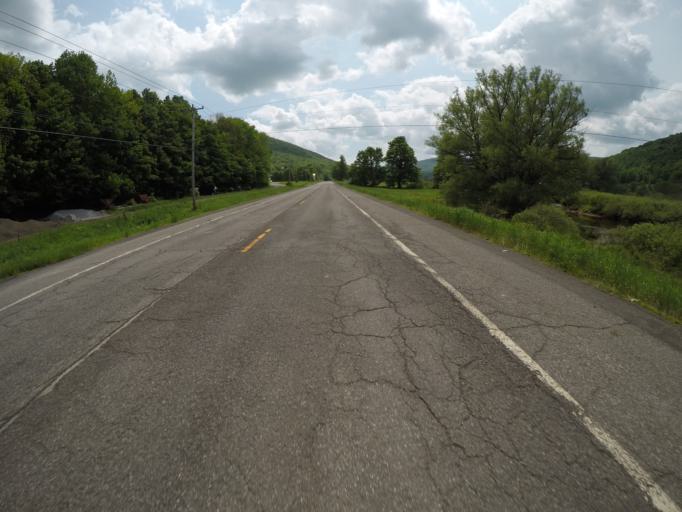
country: US
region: New York
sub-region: Delaware County
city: Stamford
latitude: 42.2722
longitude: -74.5759
